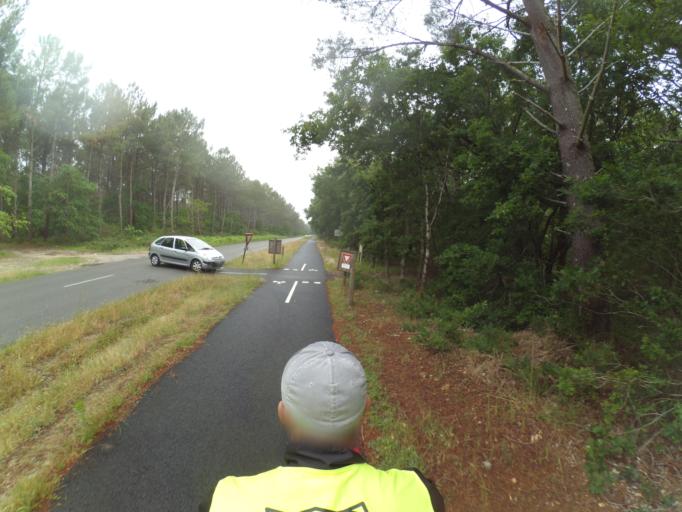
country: FR
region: Aquitaine
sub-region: Departement des Landes
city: Mimizan
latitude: 44.2373
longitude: -1.2153
